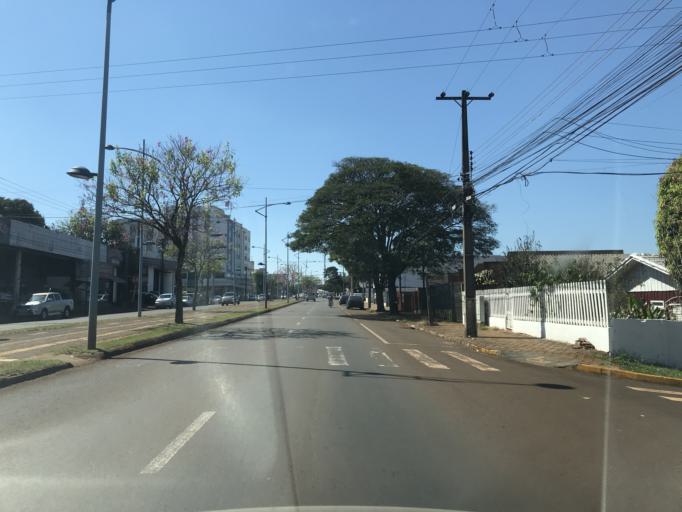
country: BR
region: Parana
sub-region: Toledo
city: Toledo
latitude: -24.7258
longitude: -53.7287
